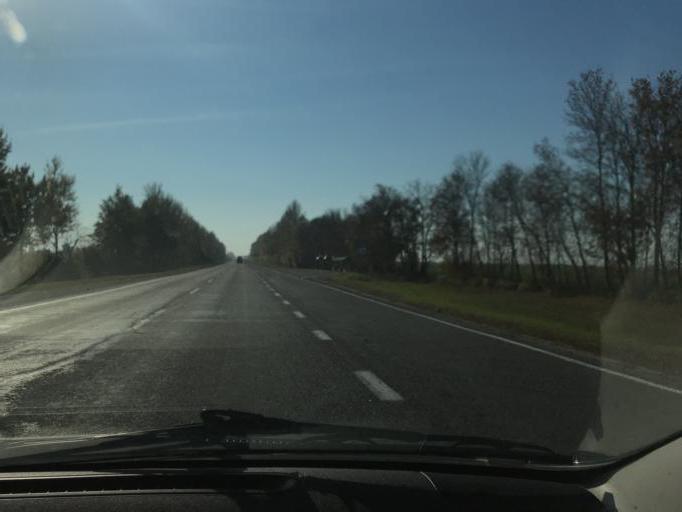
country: BY
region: Minsk
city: Salihorsk
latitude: 52.9021
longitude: 27.4763
